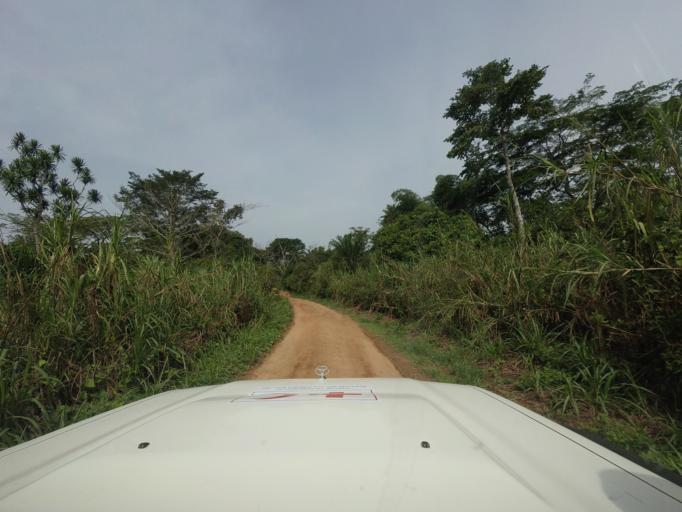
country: GN
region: Nzerekore
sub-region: Macenta
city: Macenta
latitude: 8.4750
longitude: -9.5631
